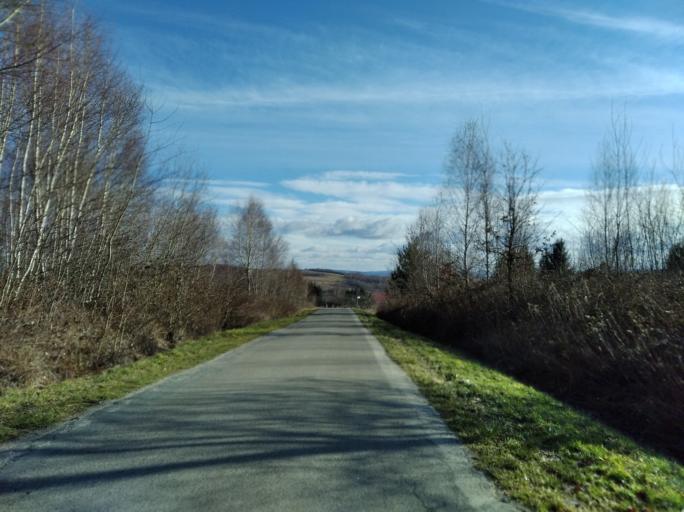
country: PL
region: Subcarpathian Voivodeship
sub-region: Powiat strzyzowski
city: Wisniowa
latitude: 49.9036
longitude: 21.6553
